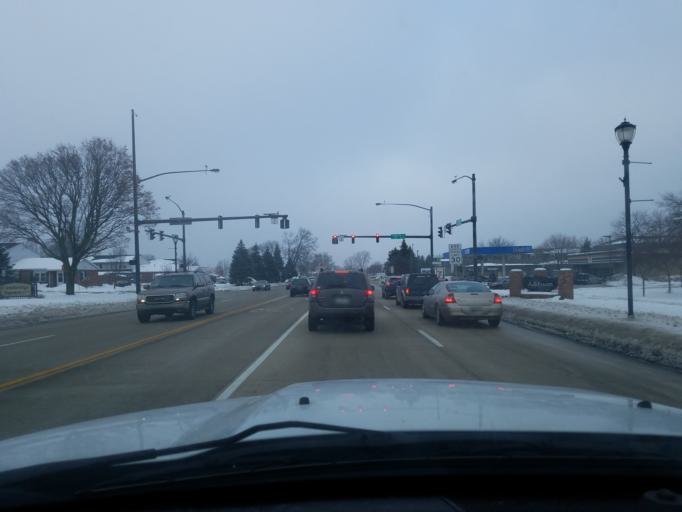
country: US
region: Indiana
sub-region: Saint Joseph County
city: Mishawaka
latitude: 41.6908
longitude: -86.1817
